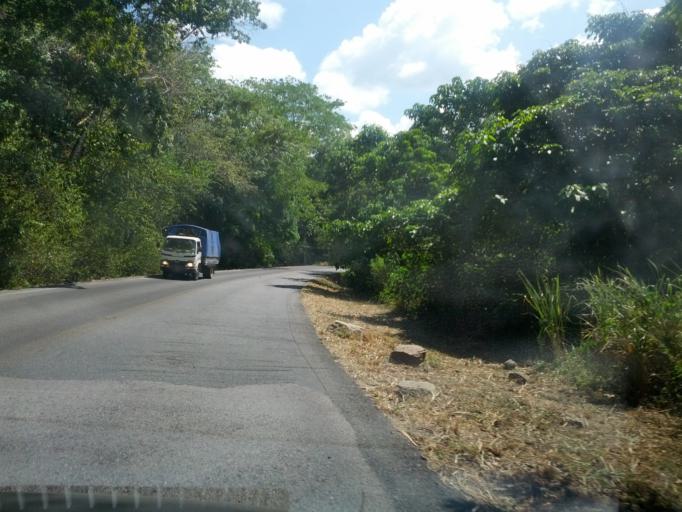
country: CR
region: Puntarenas
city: Ciudad Cortes
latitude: 8.9630
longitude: -83.3146
